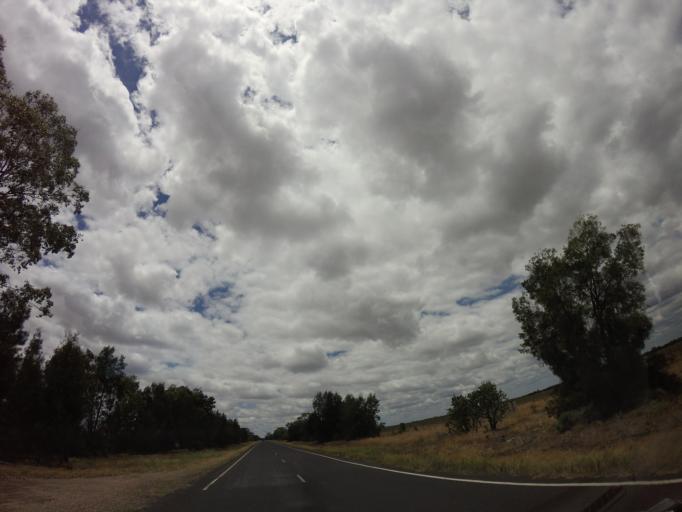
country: AU
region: Queensland
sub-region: Goondiwindi
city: Goondiwindi
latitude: -28.1687
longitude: 150.5165
